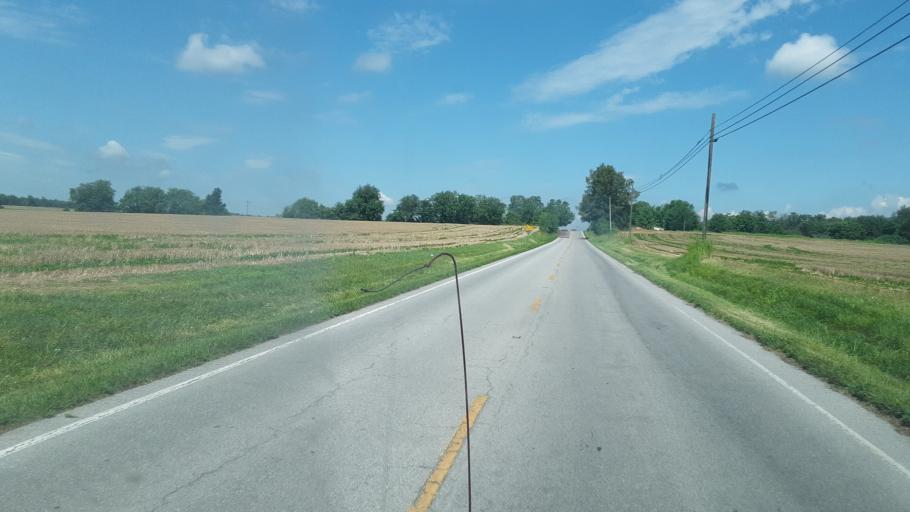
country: US
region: Kentucky
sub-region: Todd County
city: Elkton
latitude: 36.8149
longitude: -87.1770
